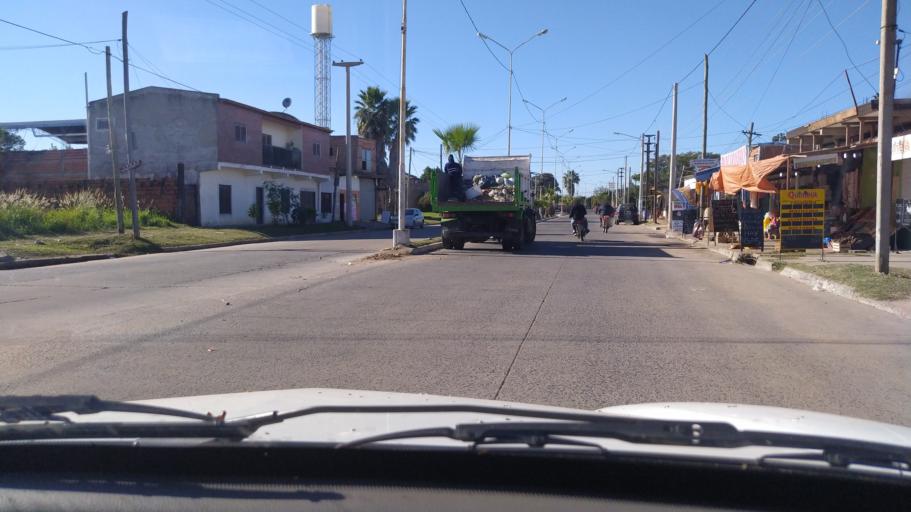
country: AR
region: Corrientes
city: Corrientes
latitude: -27.4946
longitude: -58.8037
